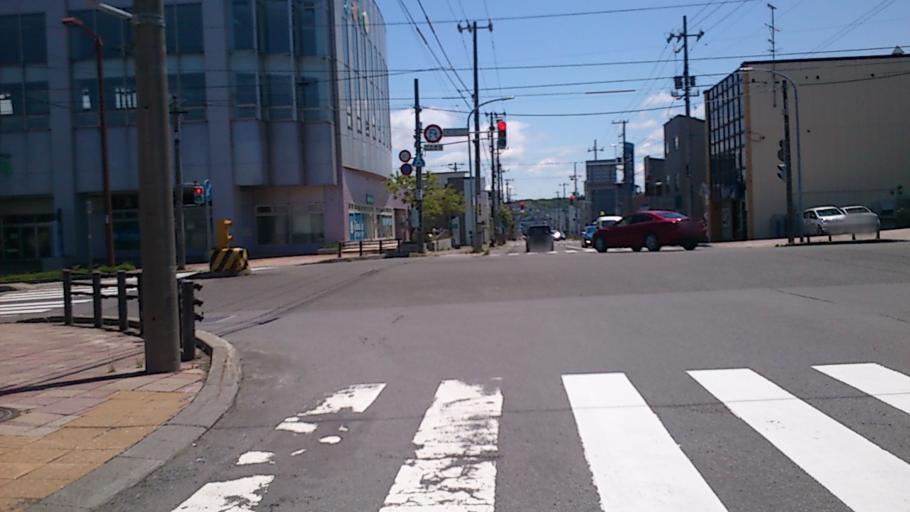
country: JP
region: Hokkaido
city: Rumoi
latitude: 43.9416
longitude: 141.6402
